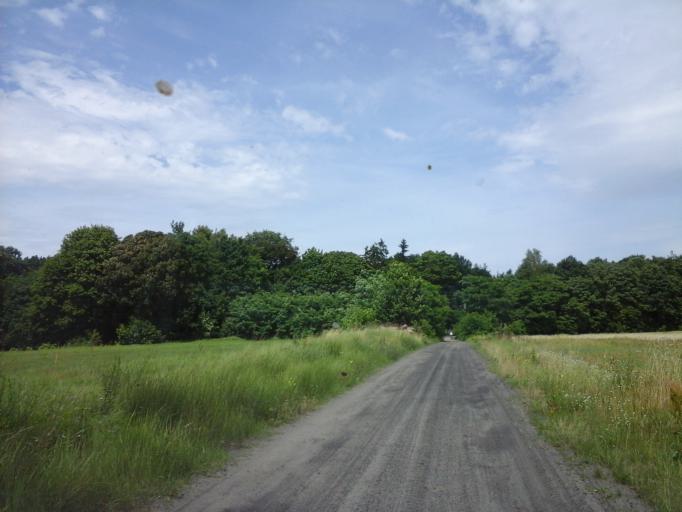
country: PL
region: Lubusz
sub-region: Powiat strzelecko-drezdenecki
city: Dobiegniew
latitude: 53.0560
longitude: 15.7593
